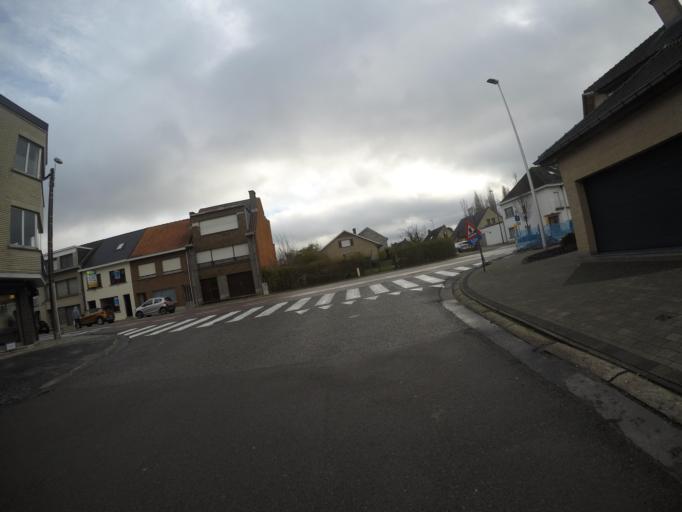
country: BE
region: Flanders
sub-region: Provincie Vlaams-Brabant
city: Liedekerke
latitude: 50.8672
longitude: 4.0854
